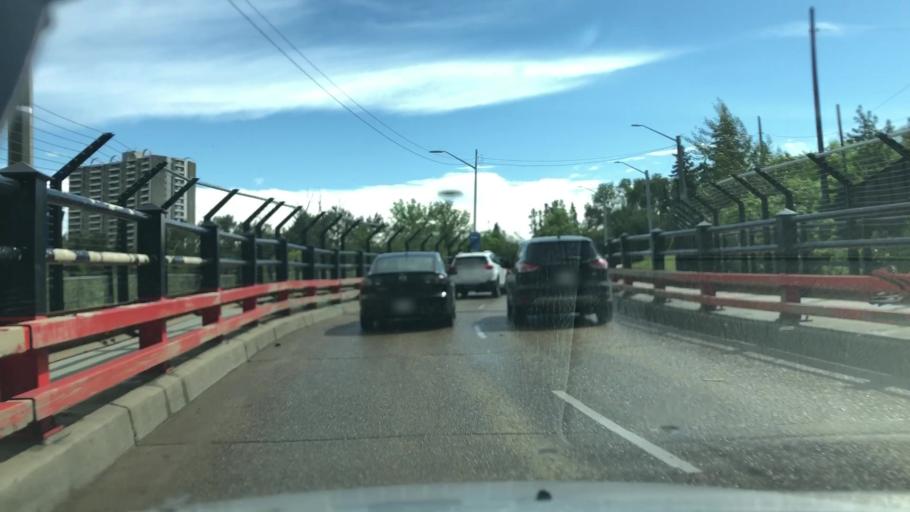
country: CA
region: Alberta
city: Edmonton
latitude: 53.5266
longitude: -113.5130
